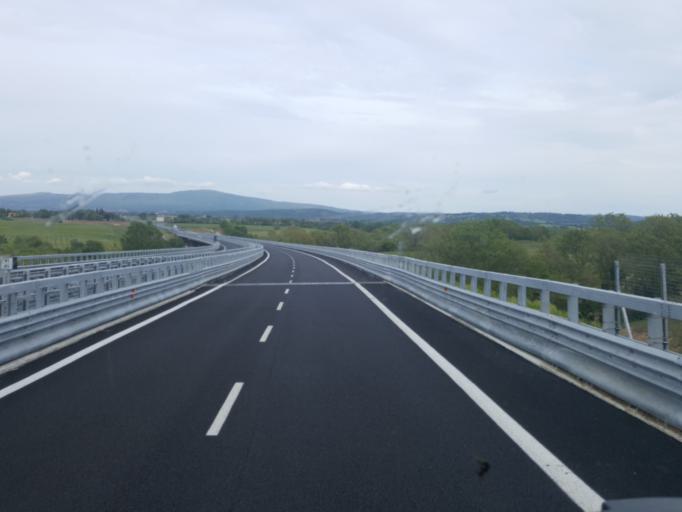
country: IT
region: Latium
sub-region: Provincia di Viterbo
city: Monte Romano
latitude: 42.2970
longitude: 11.9598
